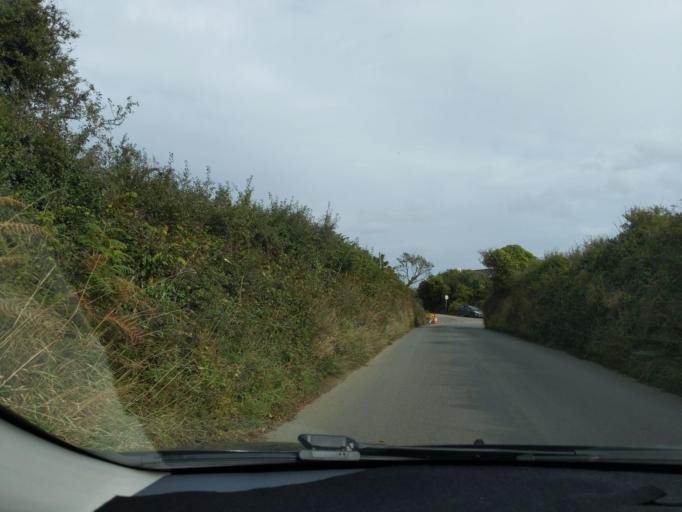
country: GB
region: England
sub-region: Cornwall
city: Mevagissey
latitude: 50.2453
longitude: -4.8020
